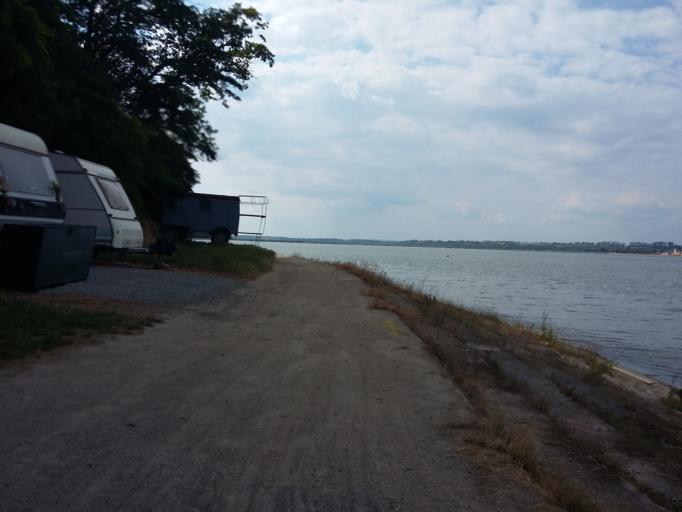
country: CZ
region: South Moravian
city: Sakvice
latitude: 48.8865
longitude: 16.6610
